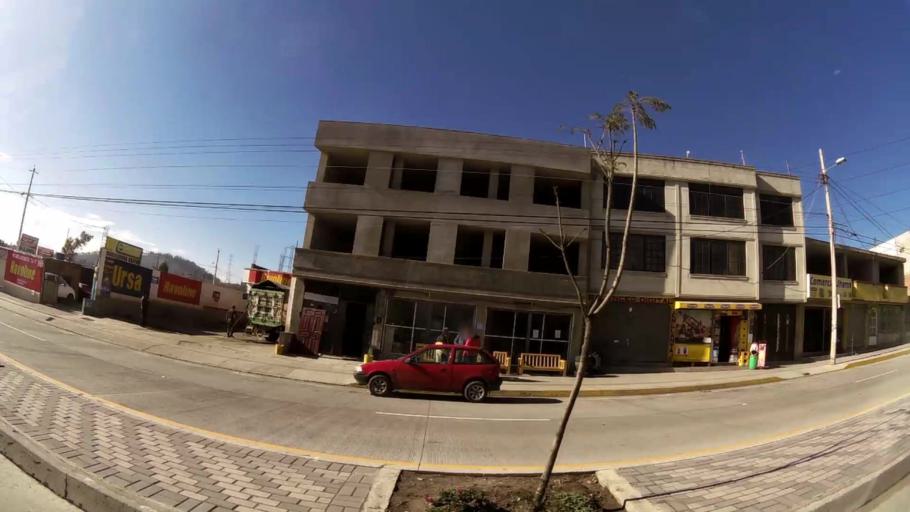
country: EC
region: Chimborazo
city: Riobamba
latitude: -1.6577
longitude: -78.6895
